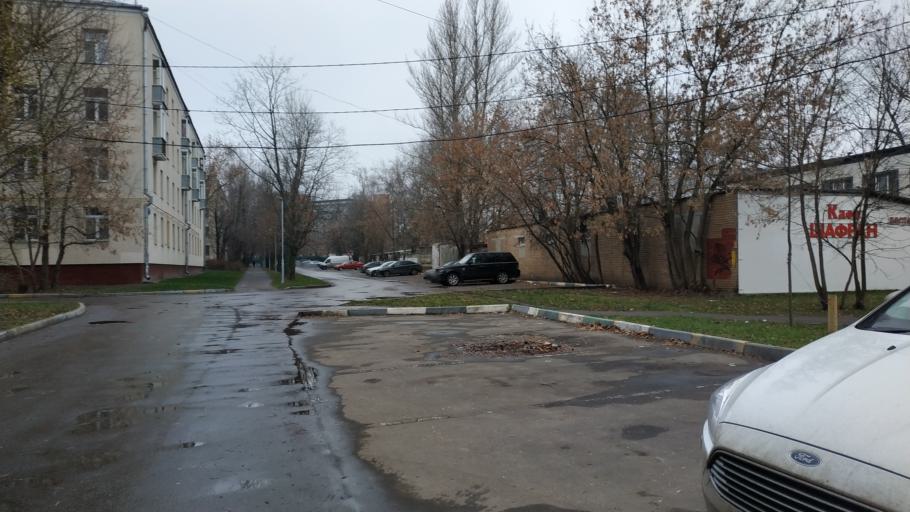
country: RU
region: Moskovskaya
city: Biryulevo Zapadnoye
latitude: 55.5935
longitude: 37.6578
